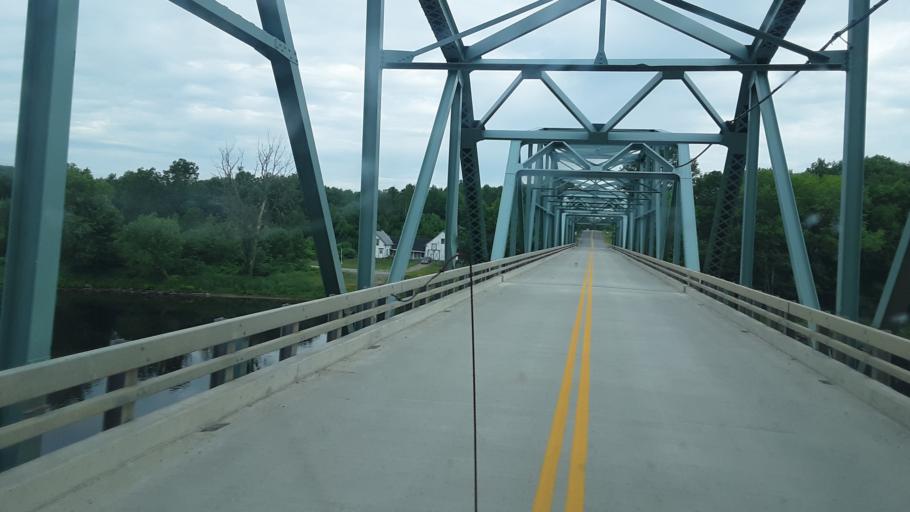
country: US
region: Maine
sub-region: Penobscot County
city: Lincoln
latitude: 45.4321
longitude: -68.4588
